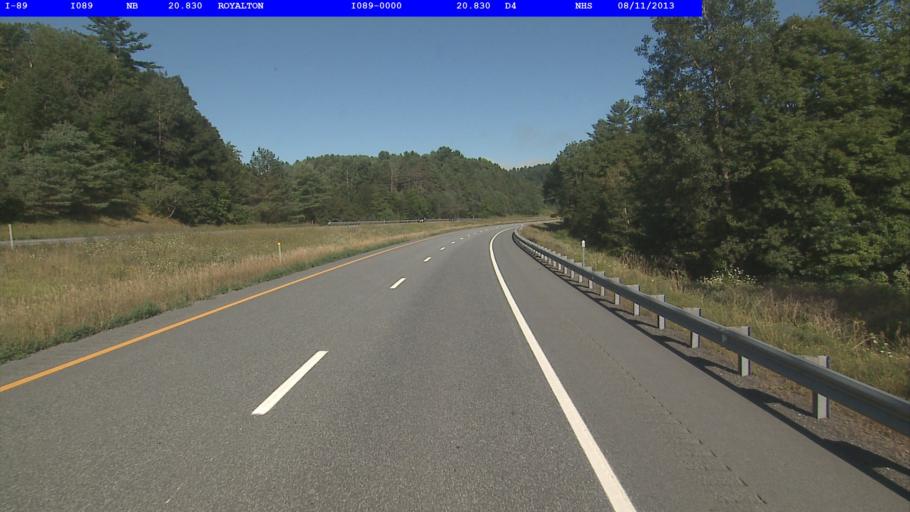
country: US
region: Vermont
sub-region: Orange County
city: Randolph
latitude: 43.8124
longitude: -72.5623
